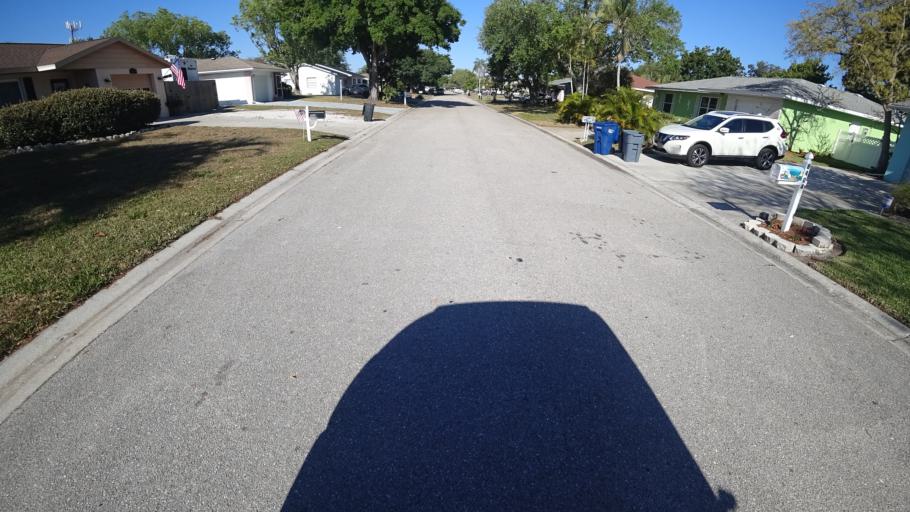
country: US
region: Florida
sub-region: Manatee County
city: Cortez
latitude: 27.4635
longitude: -82.6458
